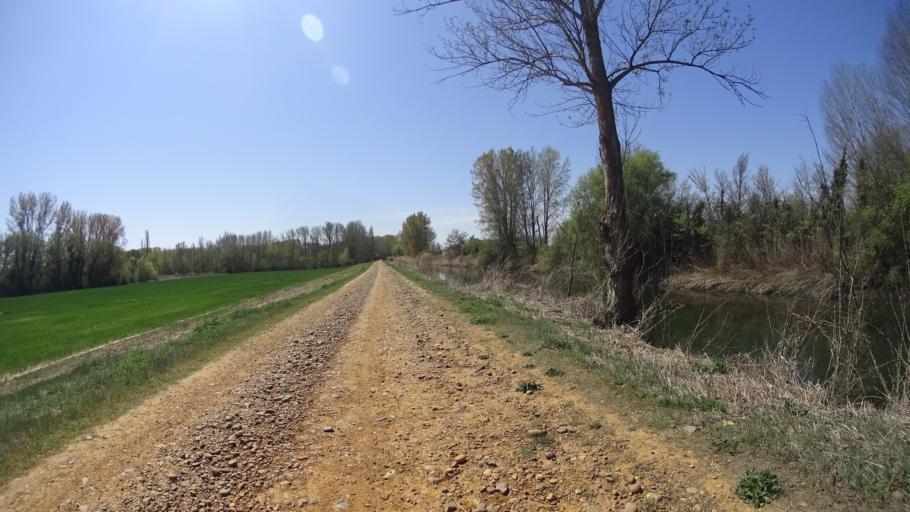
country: ES
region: Castille and Leon
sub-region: Provincia de Palencia
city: Ribas de Campos
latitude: 42.1618
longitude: -4.5343
